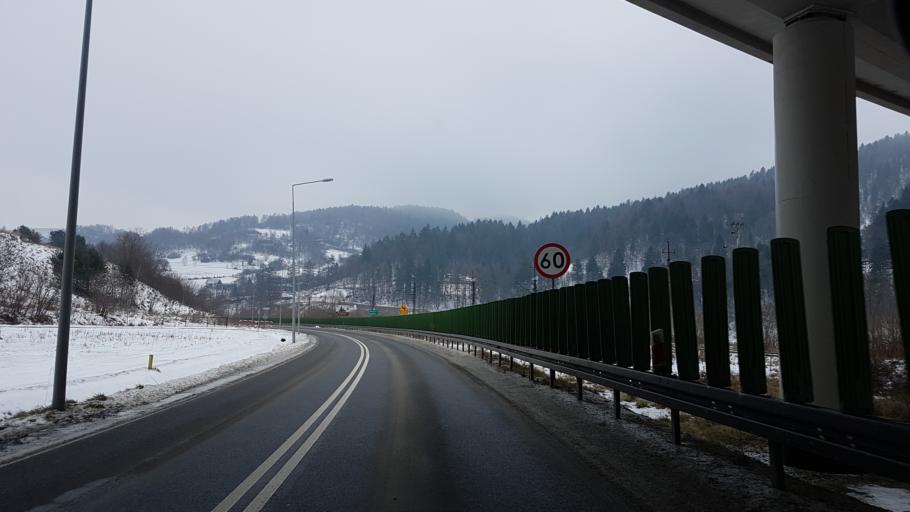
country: PL
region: Lesser Poland Voivodeship
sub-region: Powiat nowosadecki
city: Piwniczna-Zdroj
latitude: 49.4183
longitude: 20.7256
